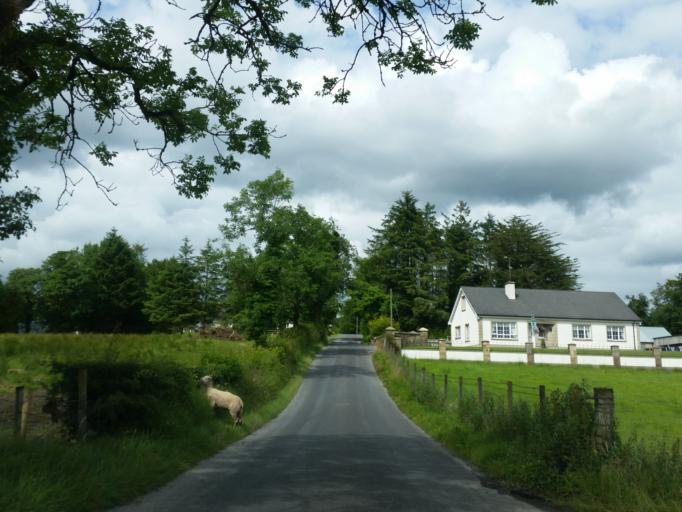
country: IE
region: Ulster
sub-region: County Monaghan
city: Clones
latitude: 54.2535
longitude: -7.2682
